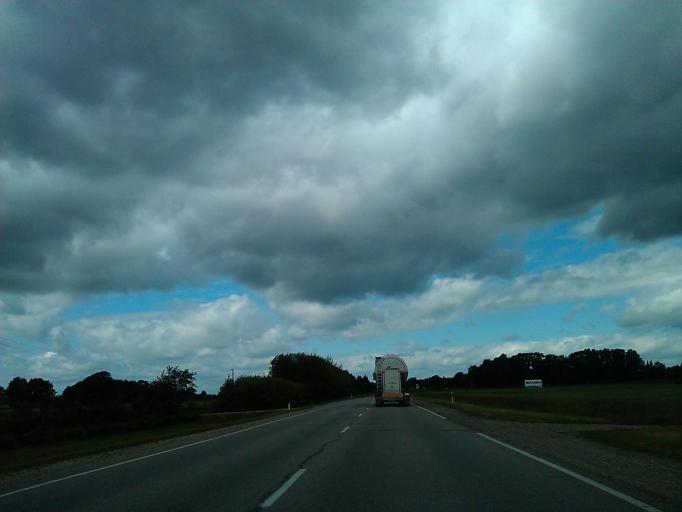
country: LV
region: Tukuma Rajons
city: Tukums
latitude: 56.9264
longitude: 23.2305
